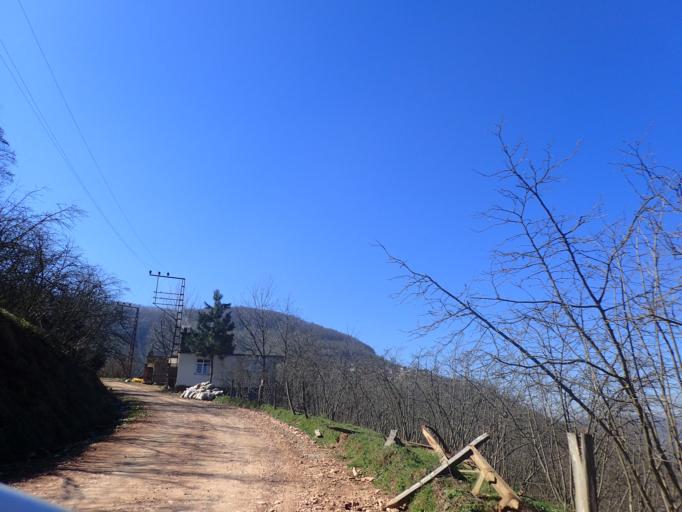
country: TR
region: Ordu
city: Catalpinar
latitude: 40.8693
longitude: 37.4935
